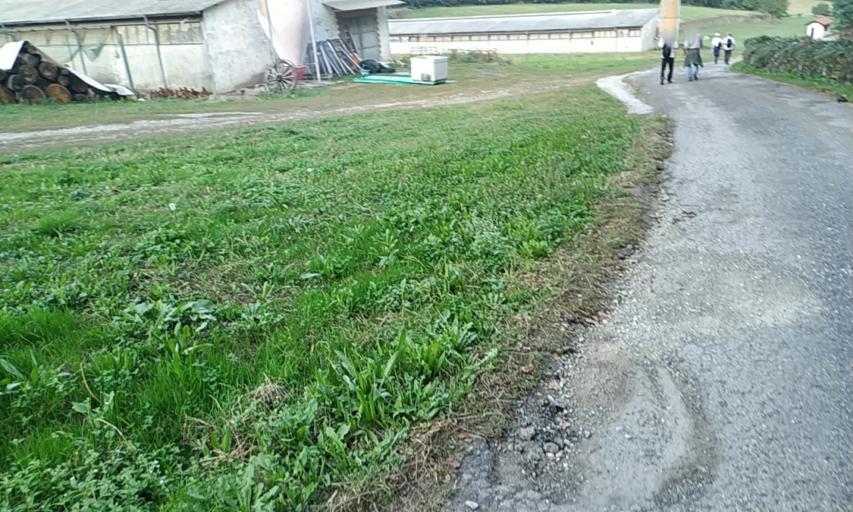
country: IT
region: Piedmont
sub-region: Provincia di Biella
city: Dorzano
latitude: 45.4401
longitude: 8.0891
